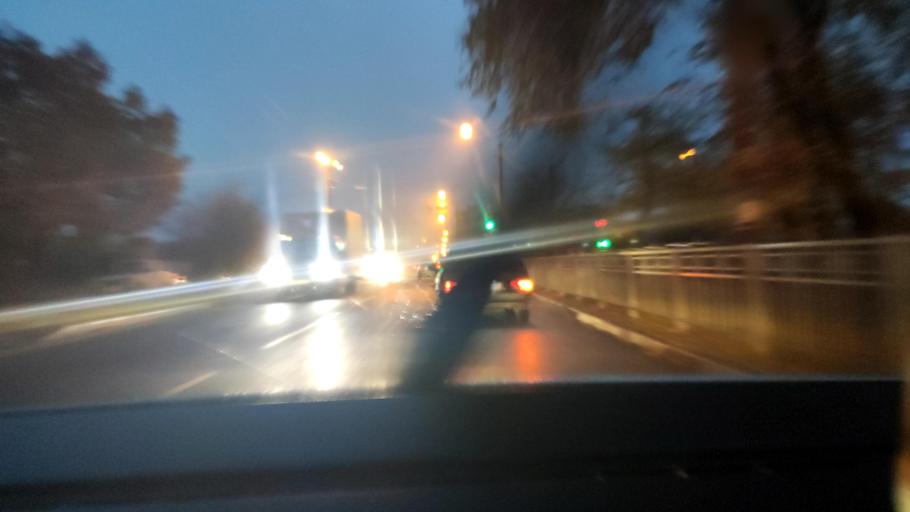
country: RU
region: Voronezj
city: Voronezh
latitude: 51.6976
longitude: 39.1567
